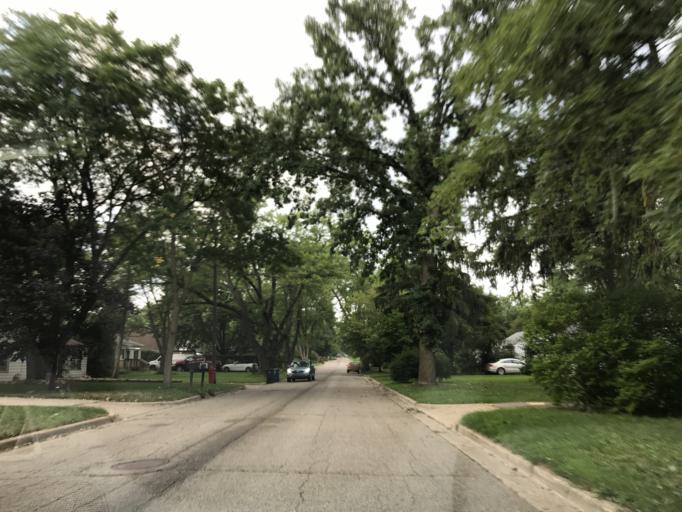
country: US
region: Michigan
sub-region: Washtenaw County
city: Ann Arbor
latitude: 42.2461
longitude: -83.6939
